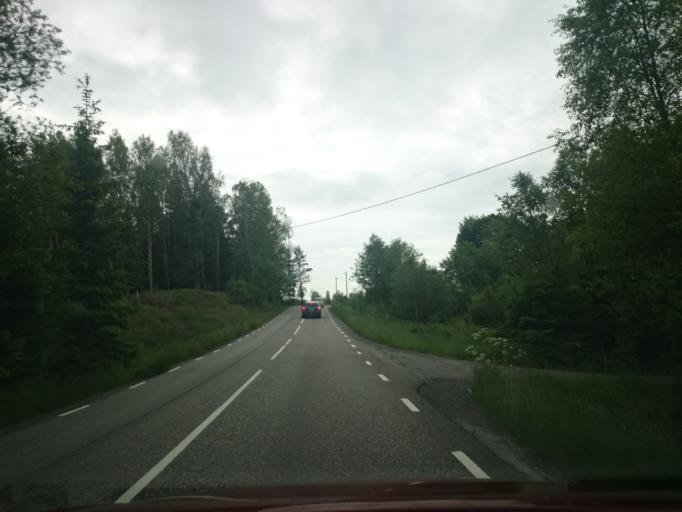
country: SE
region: Vaestra Goetaland
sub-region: Harryda Kommun
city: Hindas
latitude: 57.6998
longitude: 12.3506
